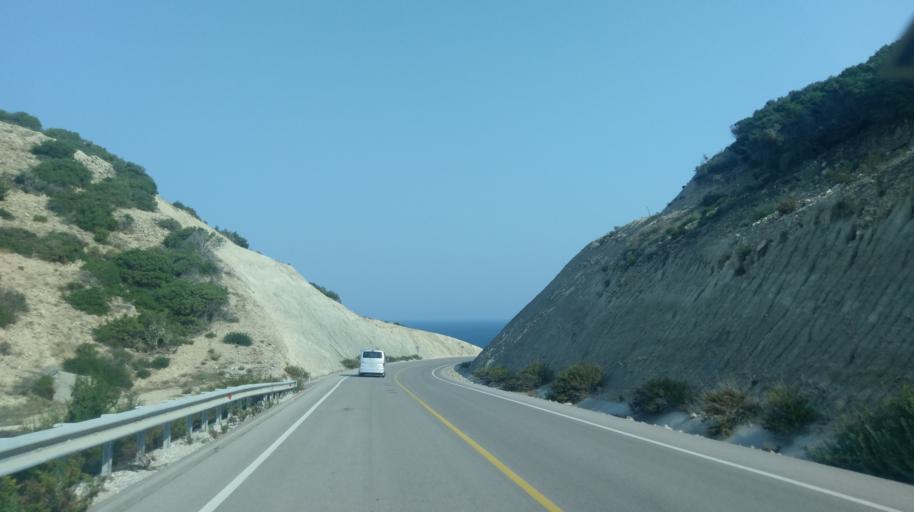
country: CY
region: Ammochostos
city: Leonarisso
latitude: 35.4629
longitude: 34.0212
